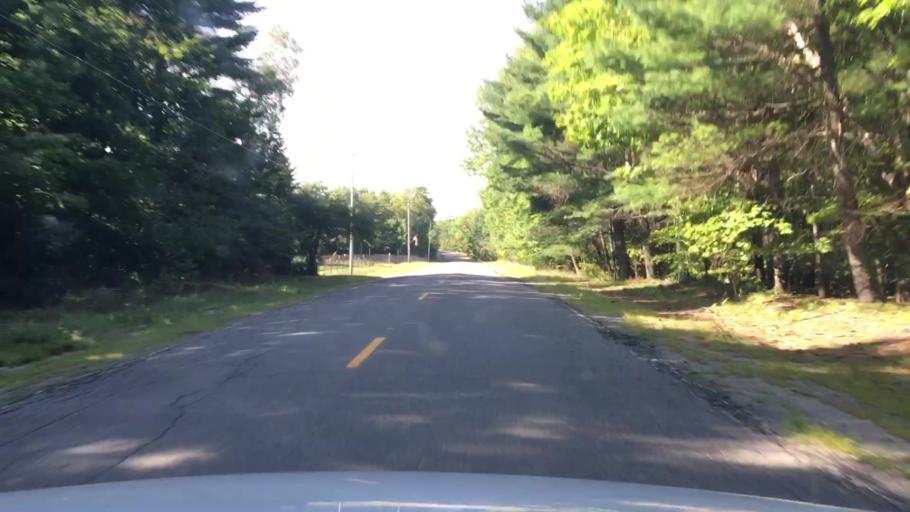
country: US
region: Maine
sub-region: Penobscot County
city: Enfield
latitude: 45.2216
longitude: -68.5370
